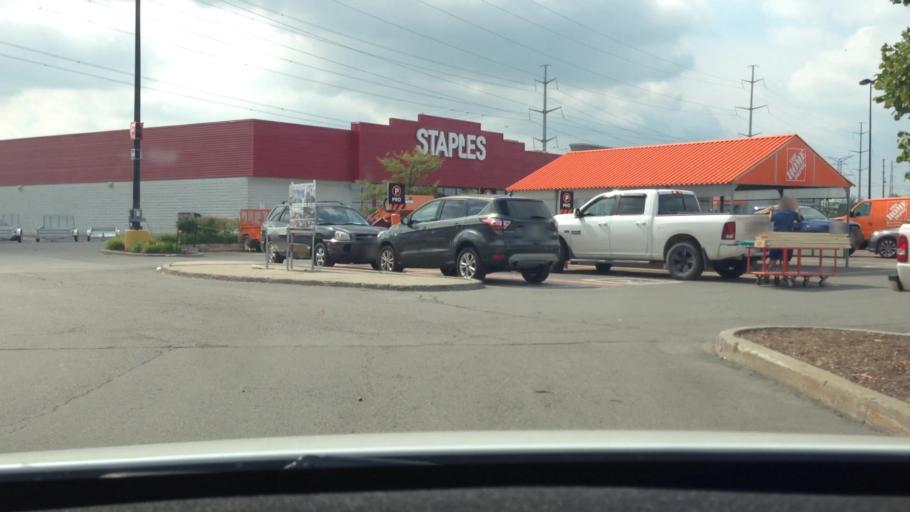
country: CA
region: Ontario
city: Clarence-Rockland
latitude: 45.4598
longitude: -75.4842
